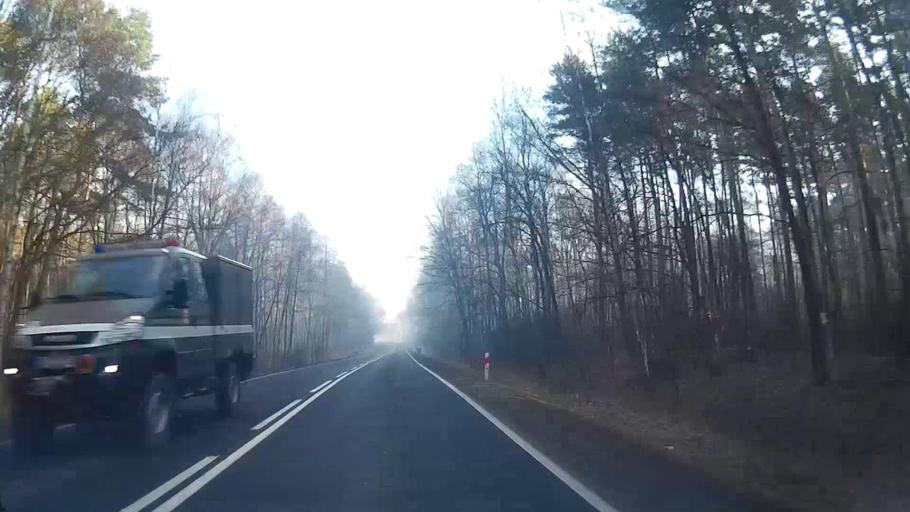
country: PL
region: Lesser Poland Voivodeship
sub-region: Powiat chrzanowski
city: Libiaz
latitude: 50.0825
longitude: 19.2828
